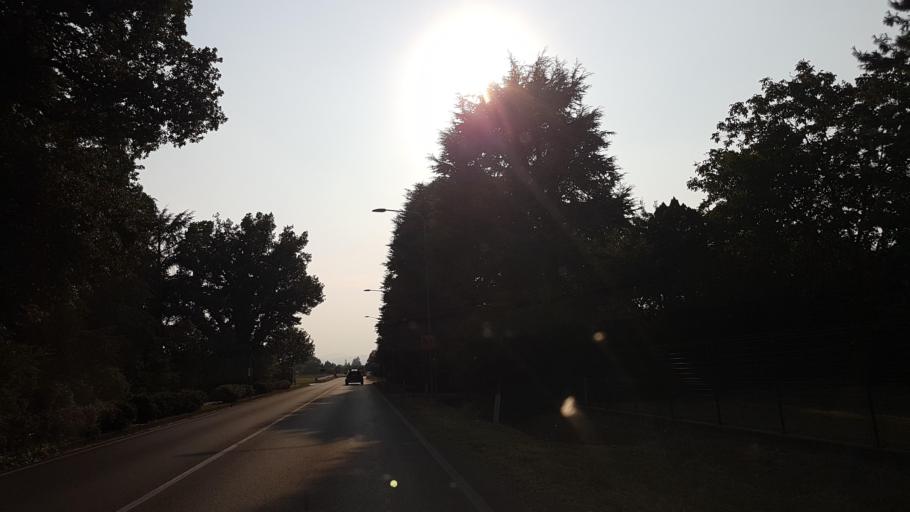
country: IT
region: Emilia-Romagna
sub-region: Provincia di Parma
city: Gaiano
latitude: 44.7224
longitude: 10.1692
